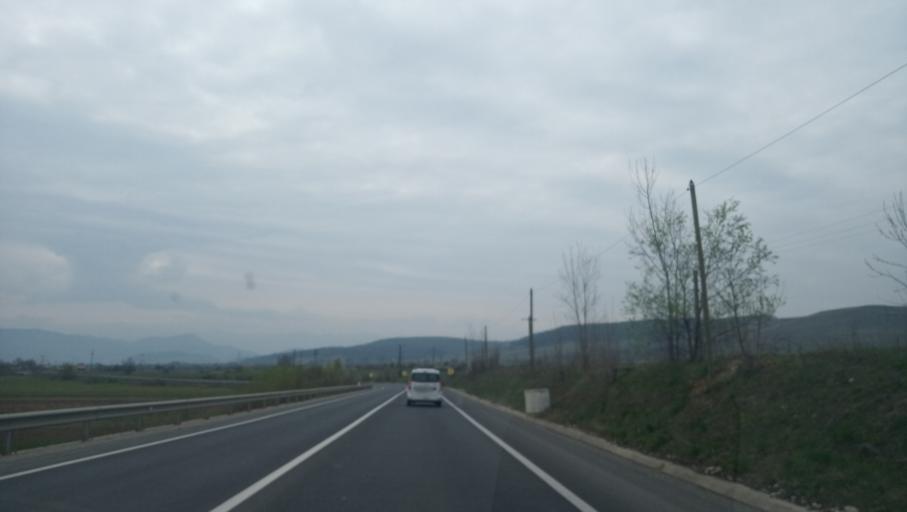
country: RO
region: Hunedoara
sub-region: Comuna Bretea Romana
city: Bretea Romana
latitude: 45.6733
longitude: 22.9944
